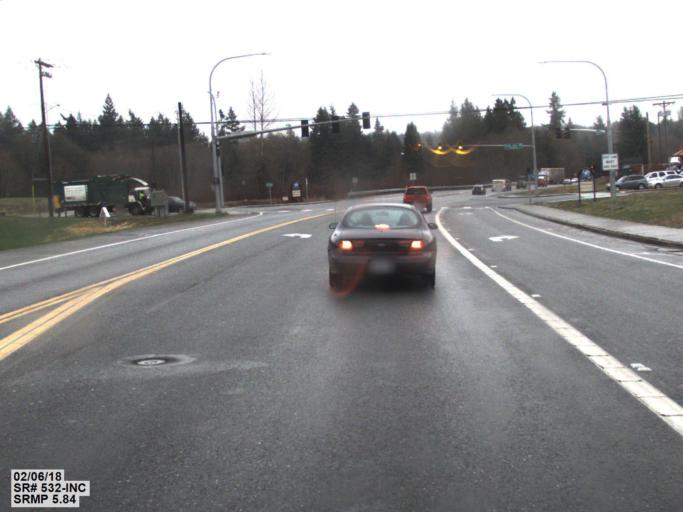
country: US
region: Washington
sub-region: Snohomish County
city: Stanwood
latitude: 48.2398
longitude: -122.3316
